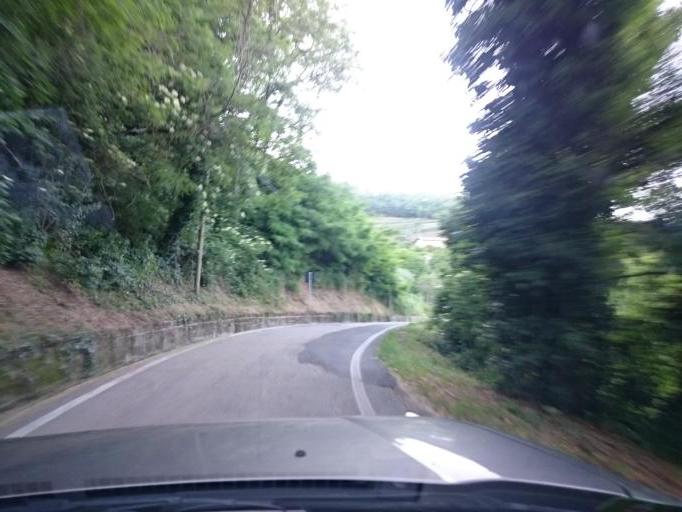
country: IT
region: Veneto
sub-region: Provincia di Padova
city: Galzignano
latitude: 45.3115
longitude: 11.6999
